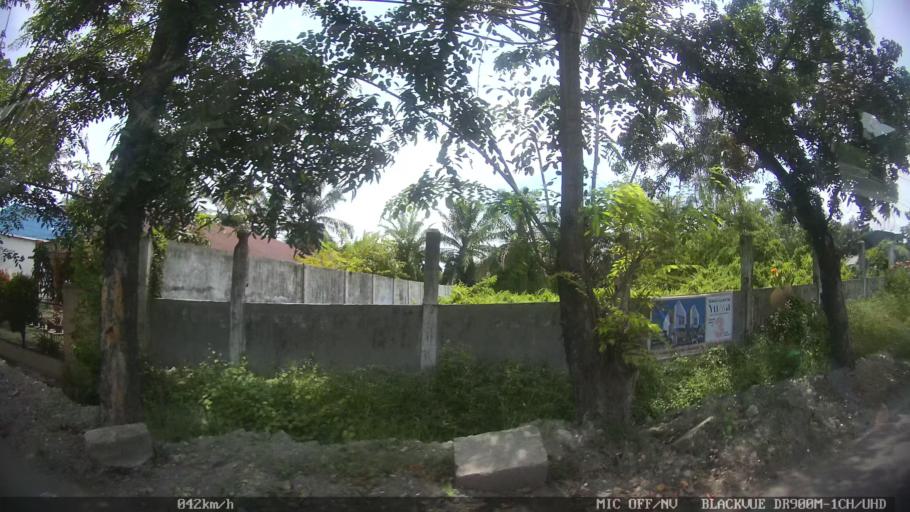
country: ID
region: North Sumatra
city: Labuhan Deli
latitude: 3.7314
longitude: 98.6759
